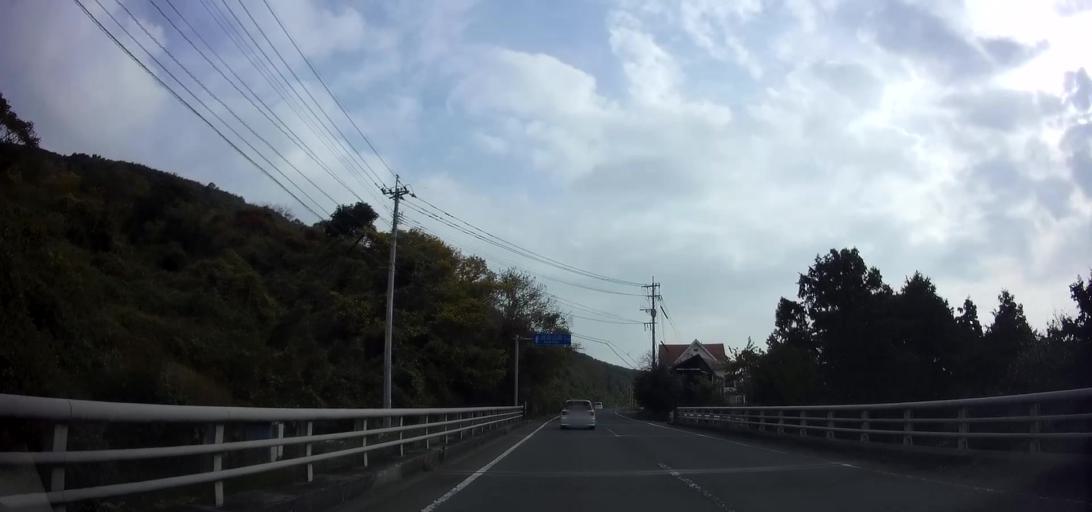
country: JP
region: Nagasaki
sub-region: Isahaya-shi
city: Isahaya
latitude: 32.7951
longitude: 130.1004
